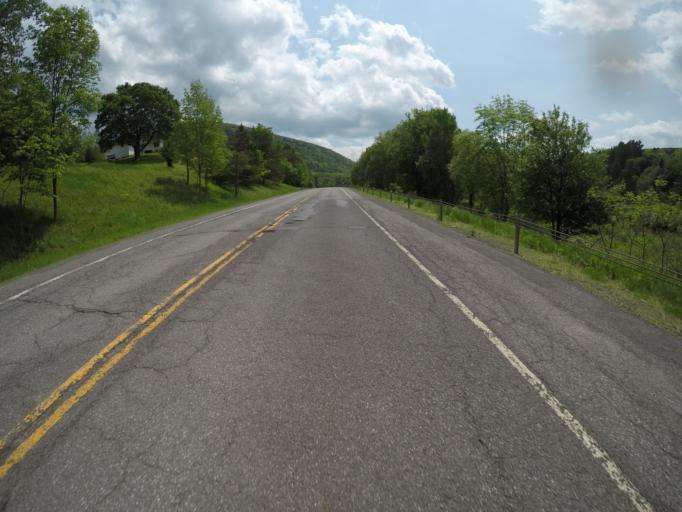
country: US
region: New York
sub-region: Delaware County
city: Stamford
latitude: 42.1845
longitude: -74.5986
